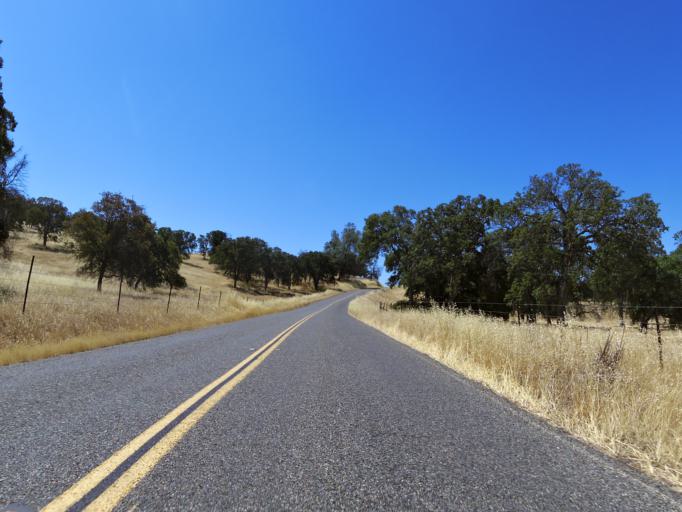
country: US
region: California
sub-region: Mariposa County
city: Mariposa
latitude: 37.4801
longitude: -120.1344
